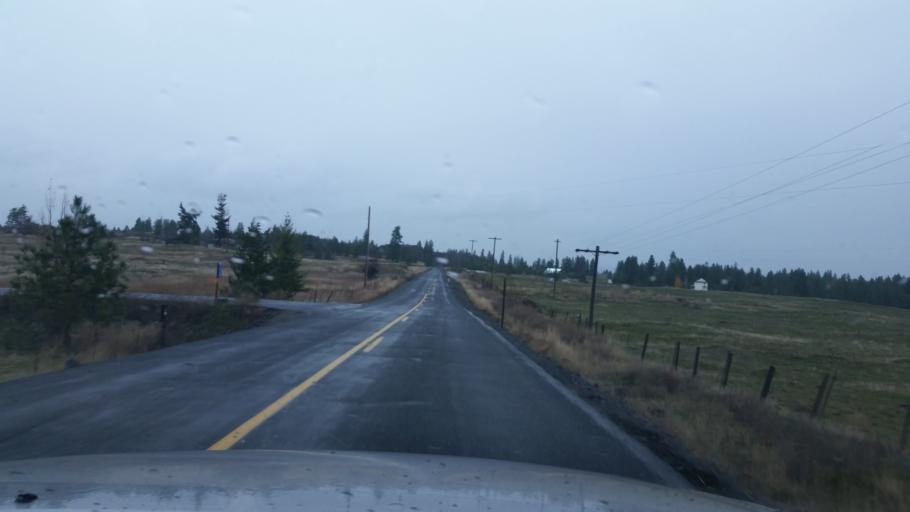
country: US
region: Washington
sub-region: Spokane County
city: Airway Heights
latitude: 47.6894
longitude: -117.5718
